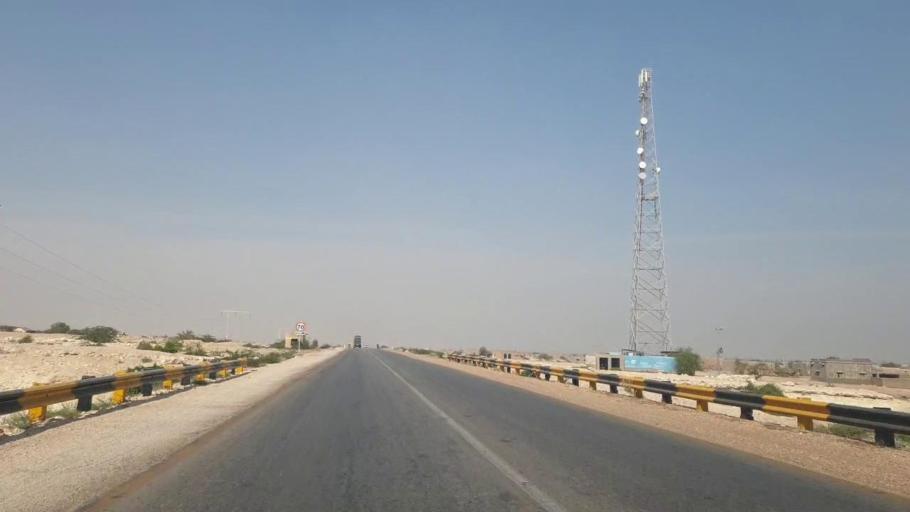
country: PK
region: Sindh
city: Hala
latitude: 25.7729
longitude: 68.2860
